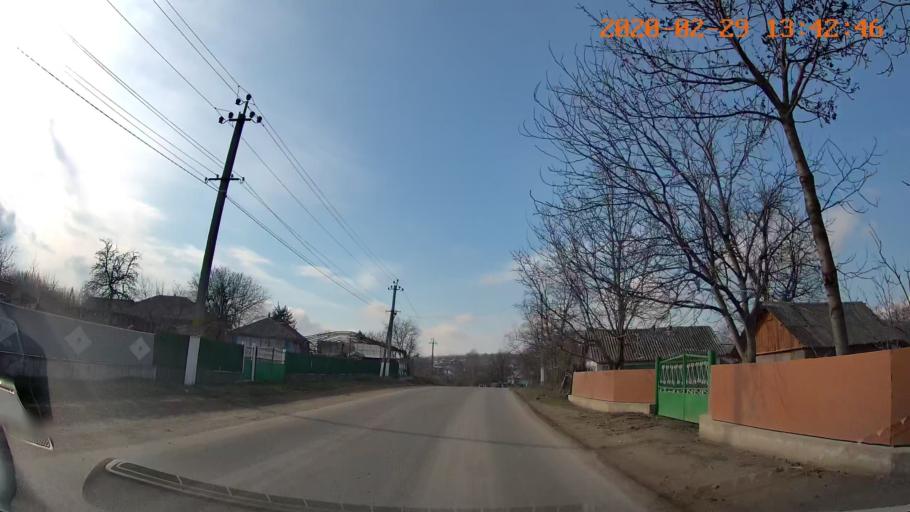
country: MD
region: Floresti
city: Leninskiy
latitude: 47.8407
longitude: 28.5427
